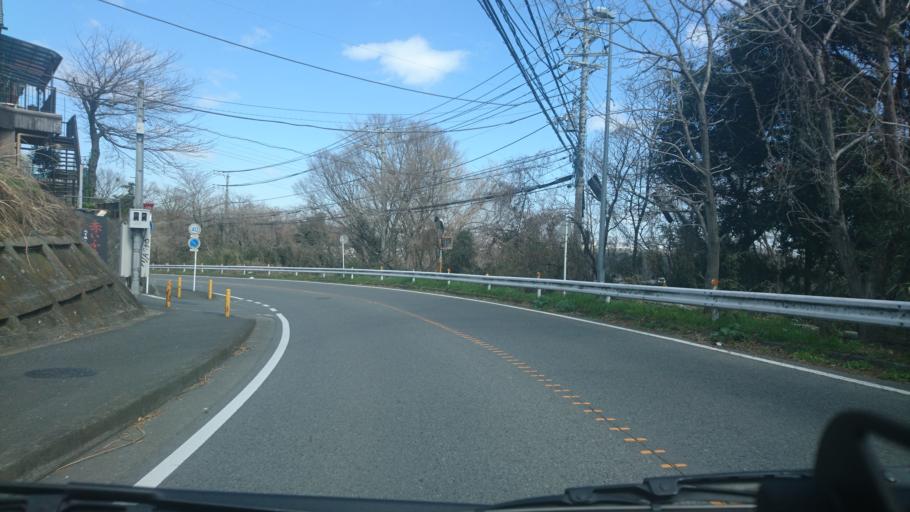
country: JP
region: Kanagawa
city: Zama
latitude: 35.5336
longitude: 139.3315
